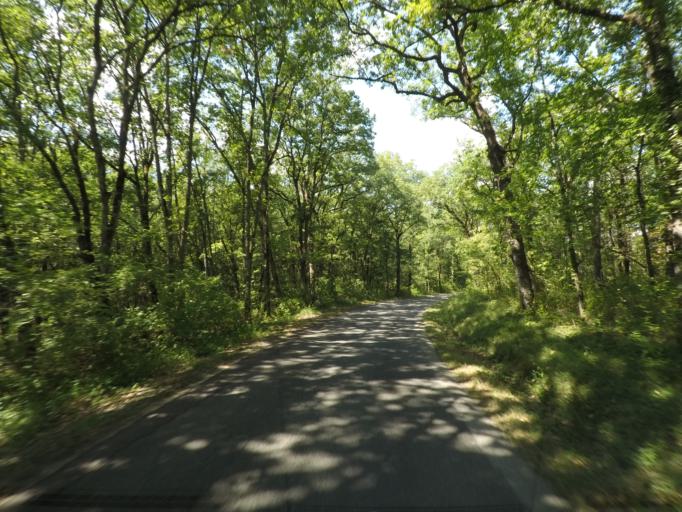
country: FR
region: Midi-Pyrenees
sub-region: Departement du Lot
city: Cahors
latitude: 44.5477
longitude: 1.5937
